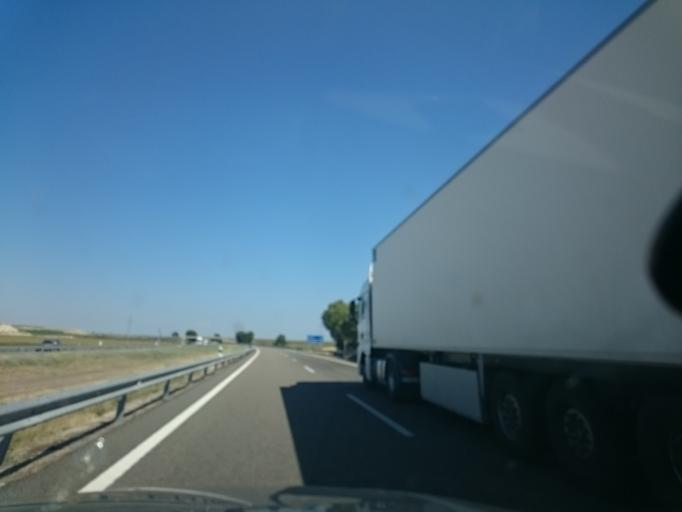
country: ES
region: Aragon
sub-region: Provincia de Zaragoza
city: Bujaraloz
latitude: 41.5187
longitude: -0.1515
